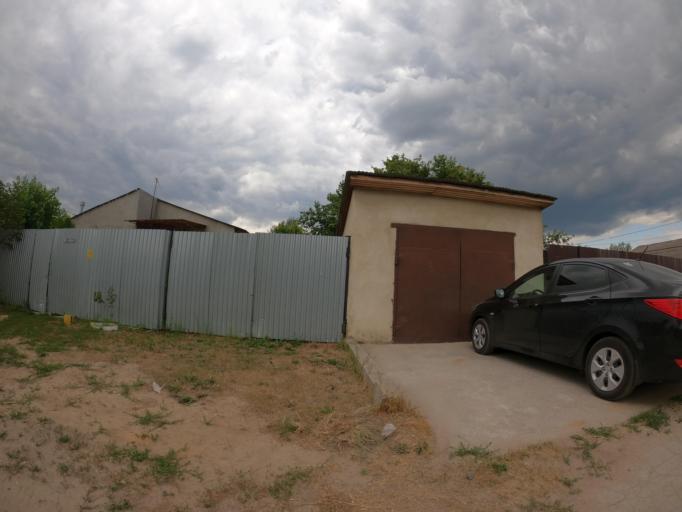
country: RU
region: Moskovskaya
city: Ramenskoye
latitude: 55.5421
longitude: 38.2269
